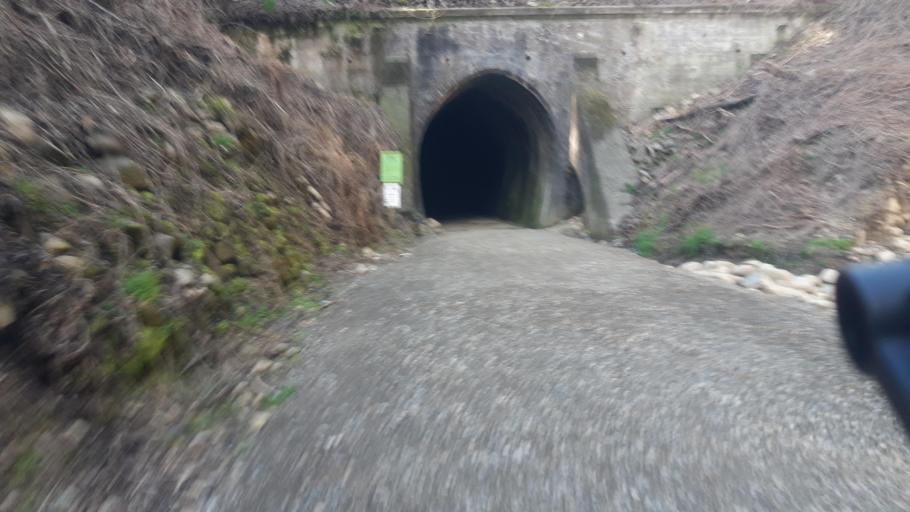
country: NZ
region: Tasman
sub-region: Tasman District
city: Wakefield
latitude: -41.4892
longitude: 172.8984
